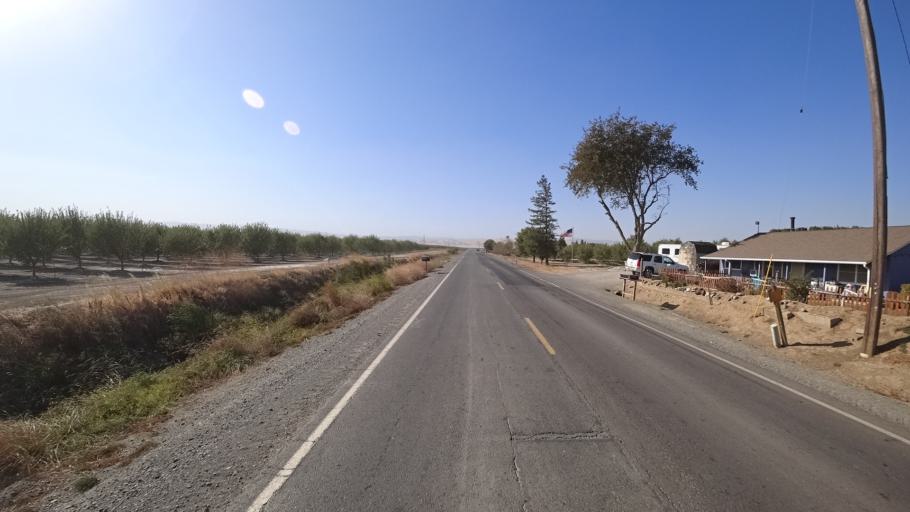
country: US
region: California
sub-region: Yolo County
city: Esparto
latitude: 38.7306
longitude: -121.9873
